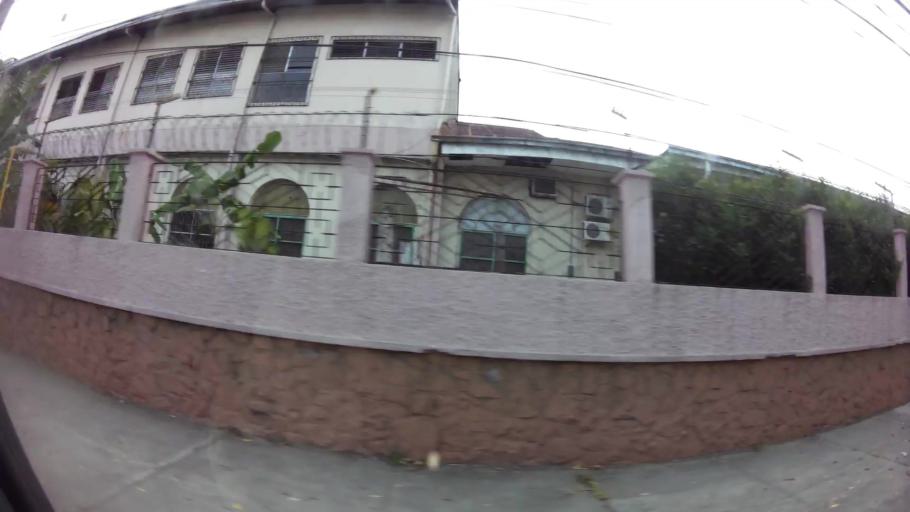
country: HN
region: Cortes
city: San Pedro Sula
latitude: 15.5092
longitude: -88.0308
